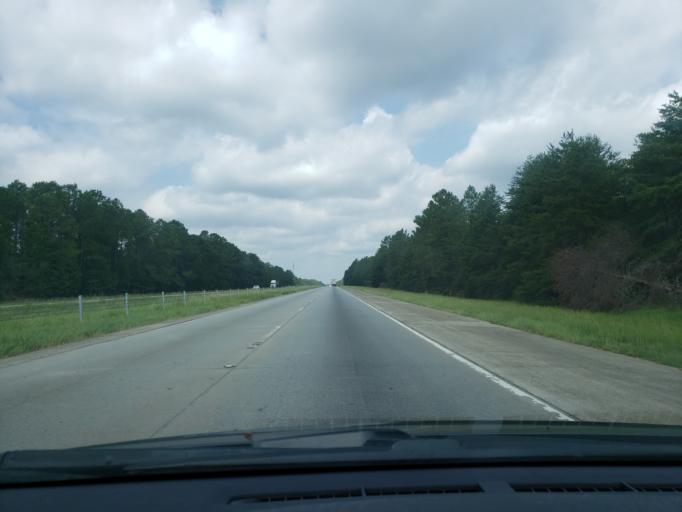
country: US
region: Georgia
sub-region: Treutlen County
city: Soperton
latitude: 32.4245
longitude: -82.4434
